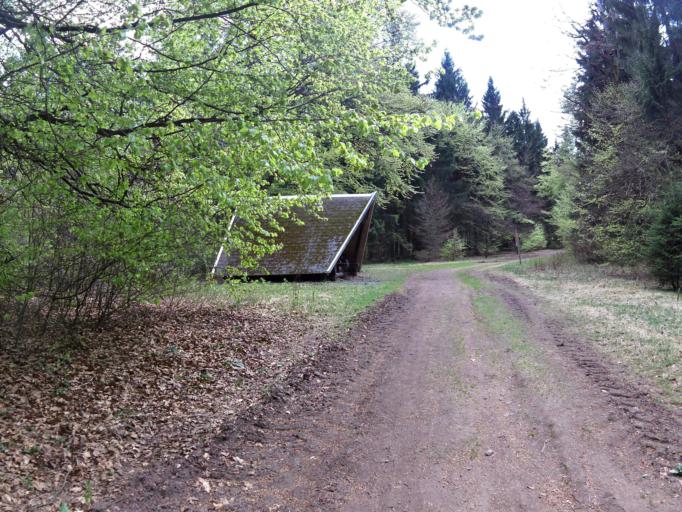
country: DE
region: Thuringia
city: Friedrichroda
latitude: 50.8242
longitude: 10.5402
